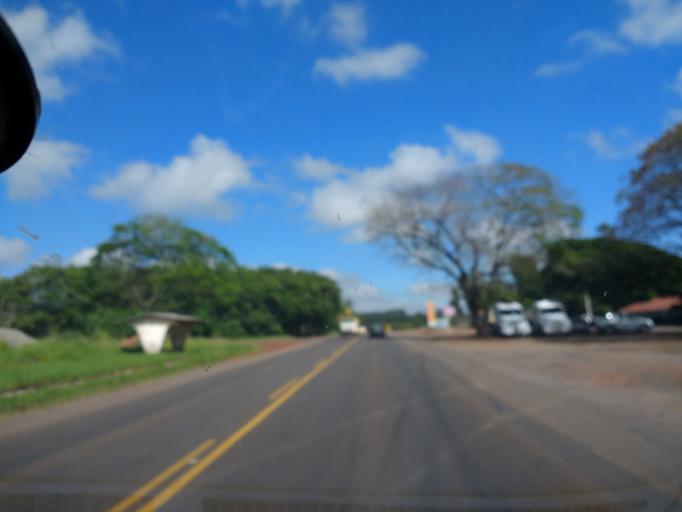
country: BR
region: Parana
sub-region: Cianorte
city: Cianorte
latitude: -23.7251
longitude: -52.6707
